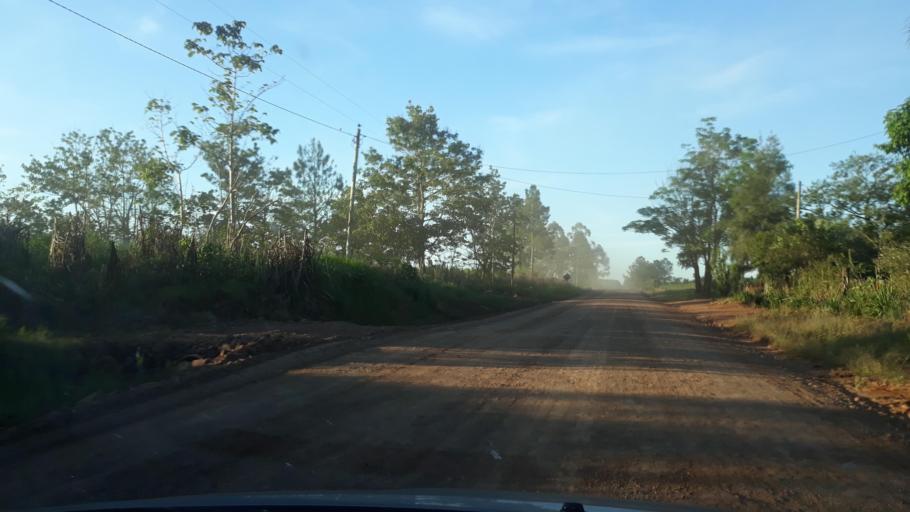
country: AR
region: Misiones
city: Ruiz de Montoya
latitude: -27.0529
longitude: -55.0044
